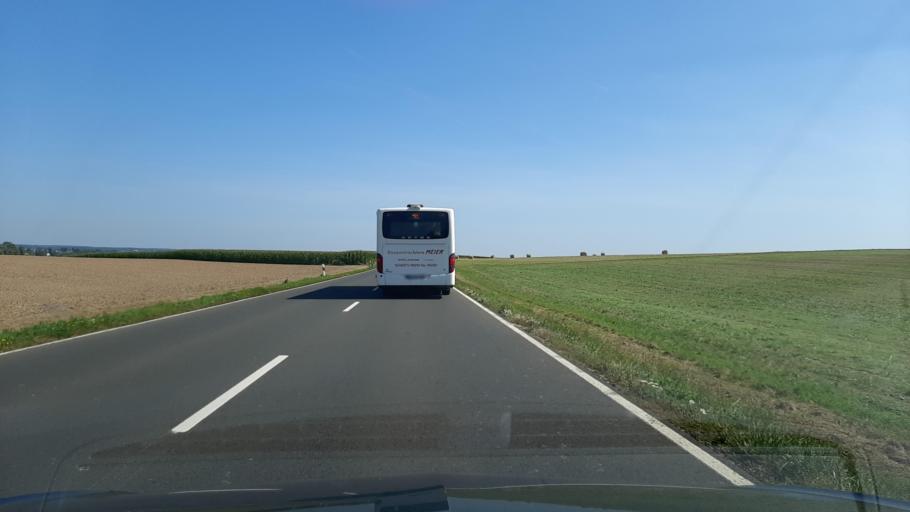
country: DE
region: Rheinland-Pfalz
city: Gondorf
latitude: 49.9783
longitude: 6.6172
